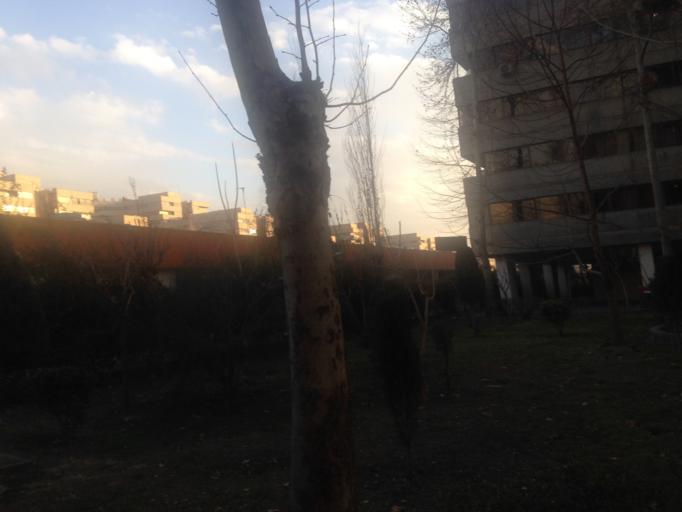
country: IR
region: Tehran
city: Tehran
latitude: 35.7123
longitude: 51.3121
